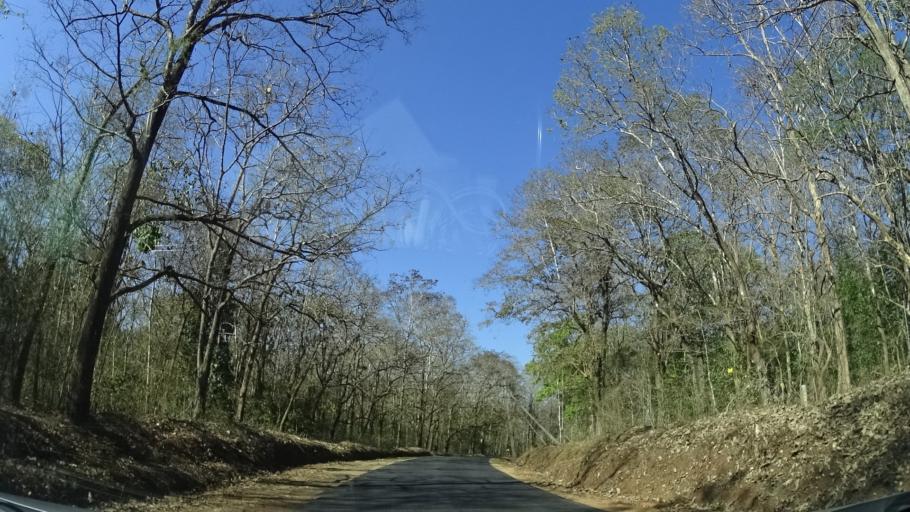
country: IN
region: Karnataka
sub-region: Chikmagalur
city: Koppa
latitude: 13.3529
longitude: 75.4924
